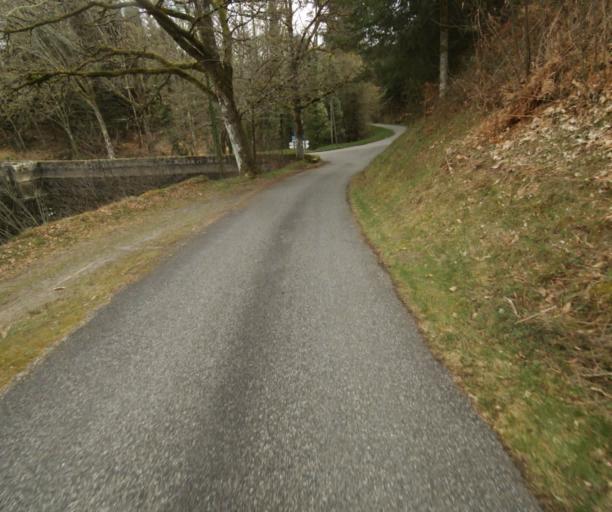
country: FR
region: Limousin
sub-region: Departement de la Correze
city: Argentat
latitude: 45.2053
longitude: 1.9613
